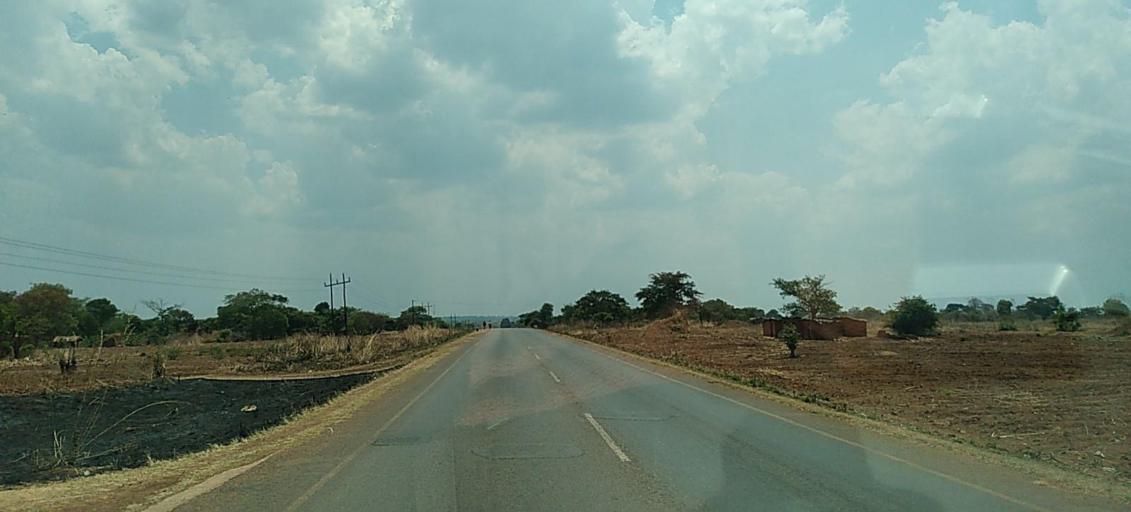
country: ZM
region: Copperbelt
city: Kalulushi
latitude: -12.8365
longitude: 27.9809
